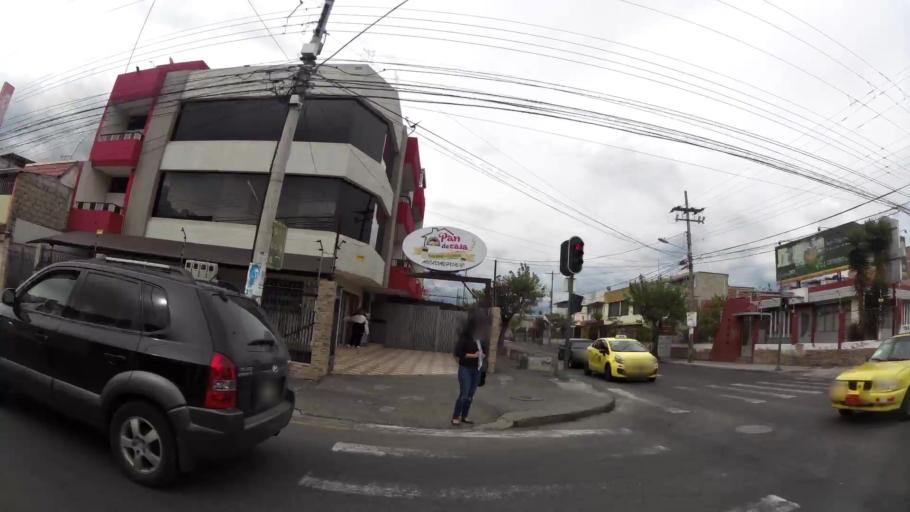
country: EC
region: Tungurahua
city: Ambato
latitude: -1.2510
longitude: -78.6314
